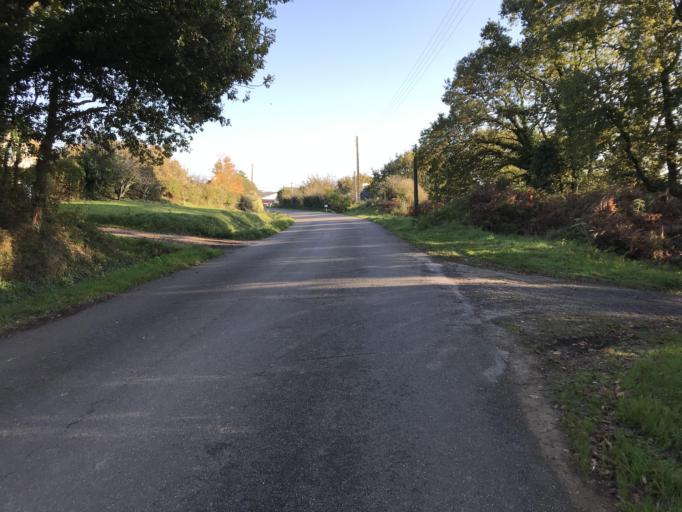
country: FR
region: Brittany
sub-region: Departement du Finistere
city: Hopital-Camfrout
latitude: 48.2997
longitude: -4.2323
